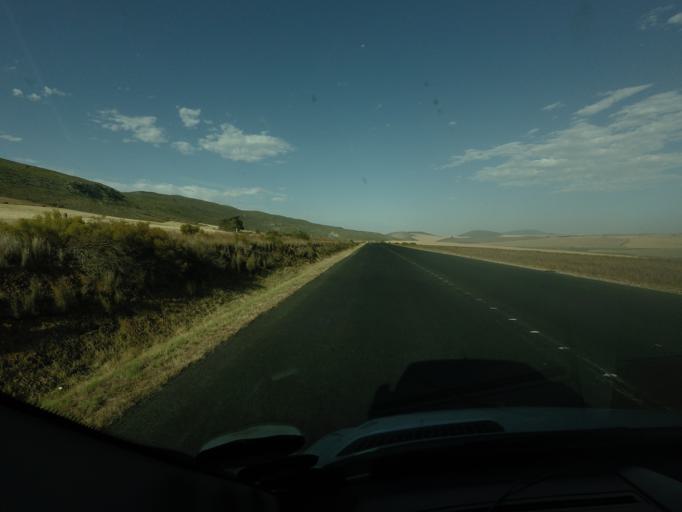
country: ZA
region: Western Cape
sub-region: Overberg District Municipality
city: Swellendam
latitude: -34.1020
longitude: 20.1951
